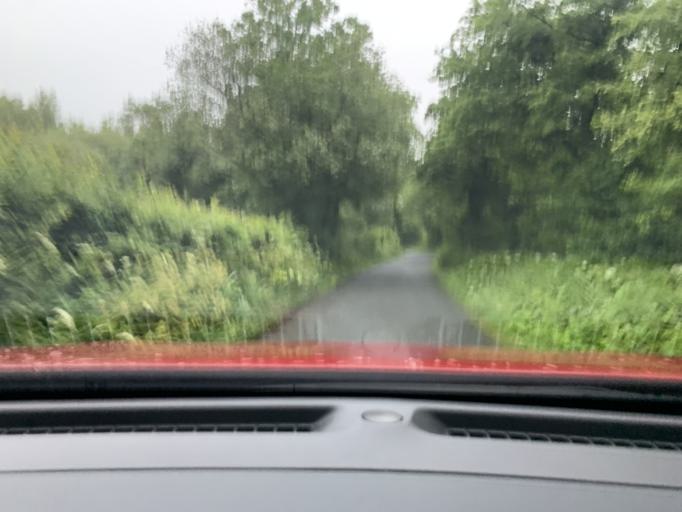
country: IE
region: Connaught
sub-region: Sligo
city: Sligo
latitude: 54.3239
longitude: -8.4477
